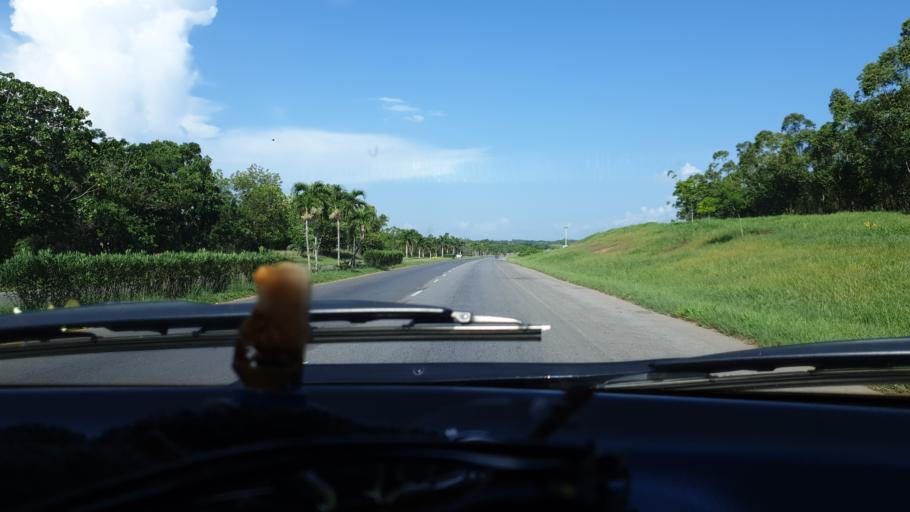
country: CU
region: Artemisa
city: San Cristobal
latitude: 22.7245
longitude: -83.0300
